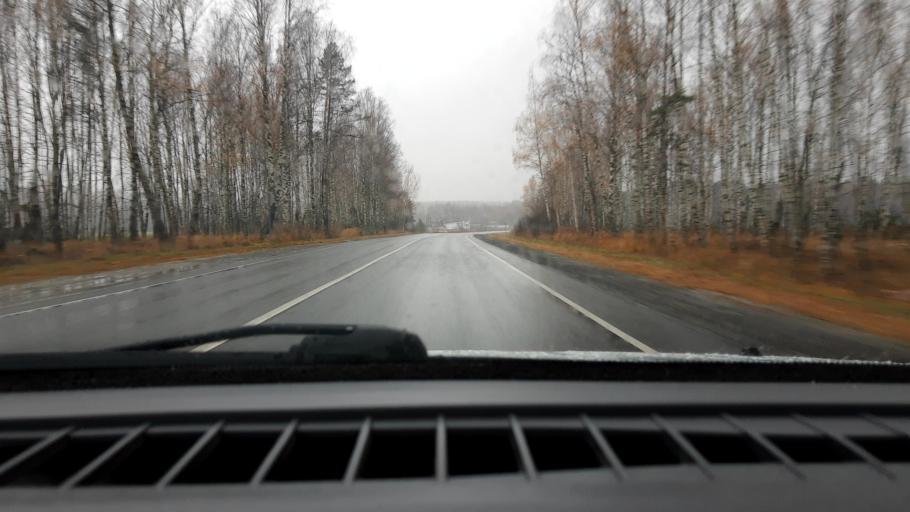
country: RU
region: Nizjnij Novgorod
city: Linda
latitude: 56.6704
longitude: 44.1408
